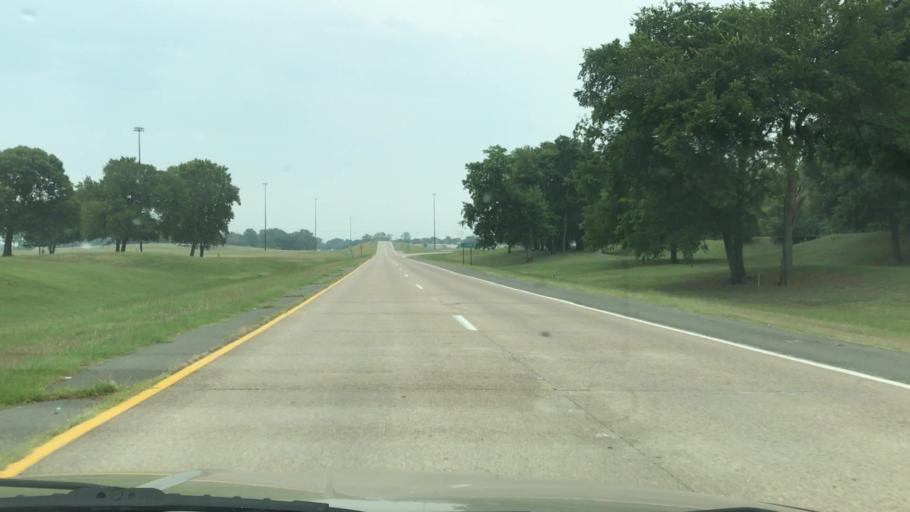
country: US
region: Louisiana
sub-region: Bossier Parish
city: Bossier City
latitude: 32.5039
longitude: -93.7201
